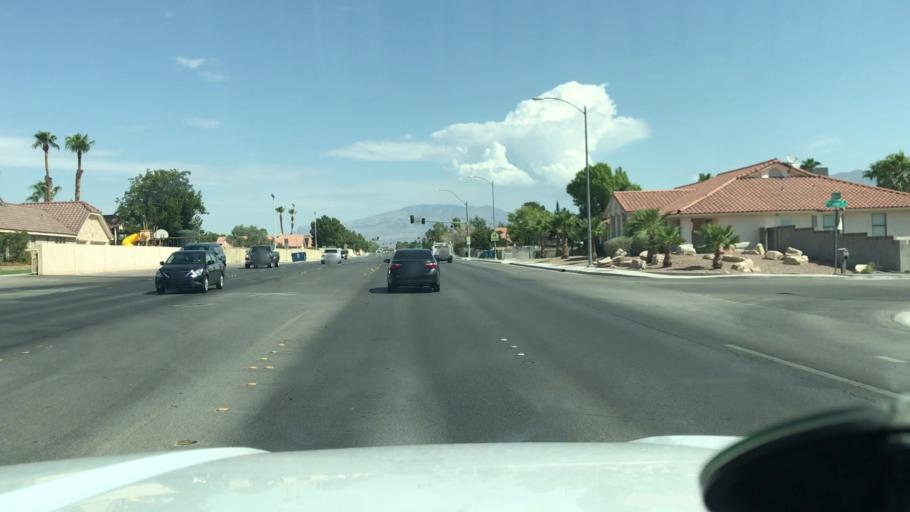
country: US
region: Nevada
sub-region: Clark County
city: Summerlin South
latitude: 36.2573
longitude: -115.2789
